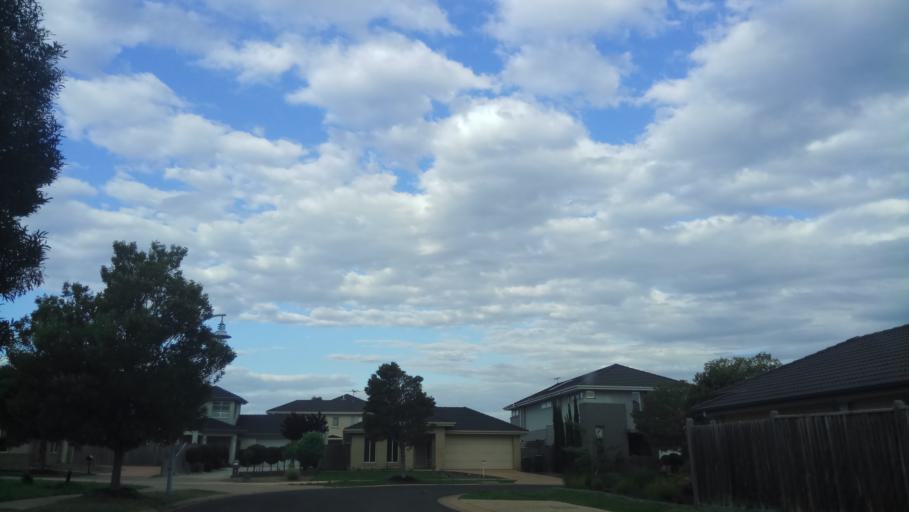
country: AU
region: Victoria
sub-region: Hobsons Bay
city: Altona Meadows
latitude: -37.8976
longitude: 144.7718
